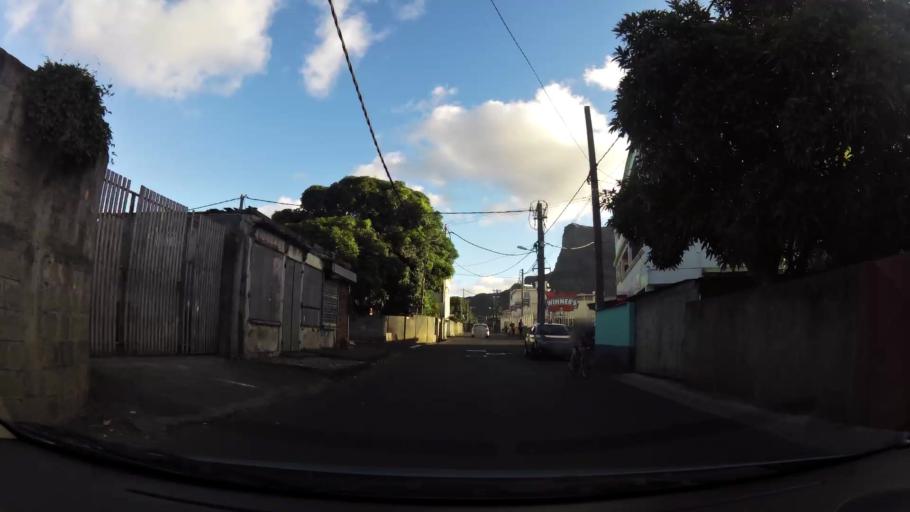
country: MU
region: Plaines Wilhems
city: Quatre Bornes
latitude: -20.2571
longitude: 57.4684
